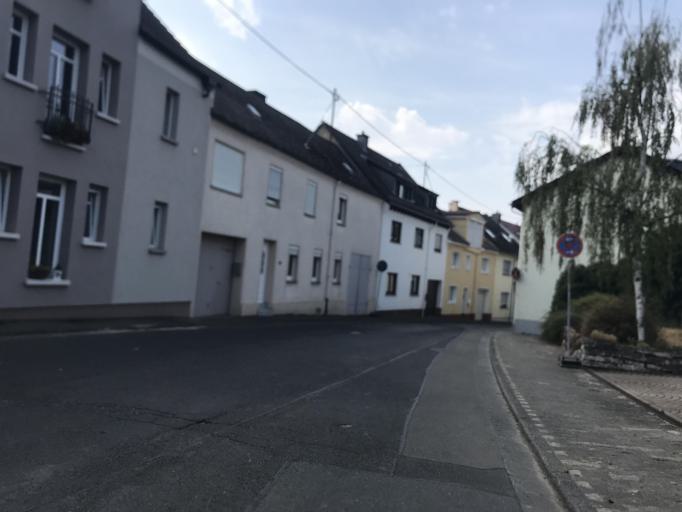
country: DE
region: Rheinland-Pfalz
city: Oestrich-Winkel
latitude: 50.0300
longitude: 8.0315
